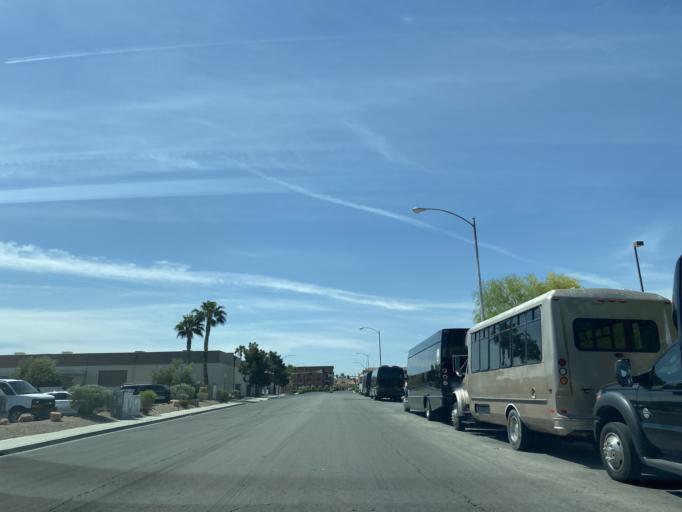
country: US
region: Nevada
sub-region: Clark County
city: Paradise
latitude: 36.0726
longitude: -115.1769
